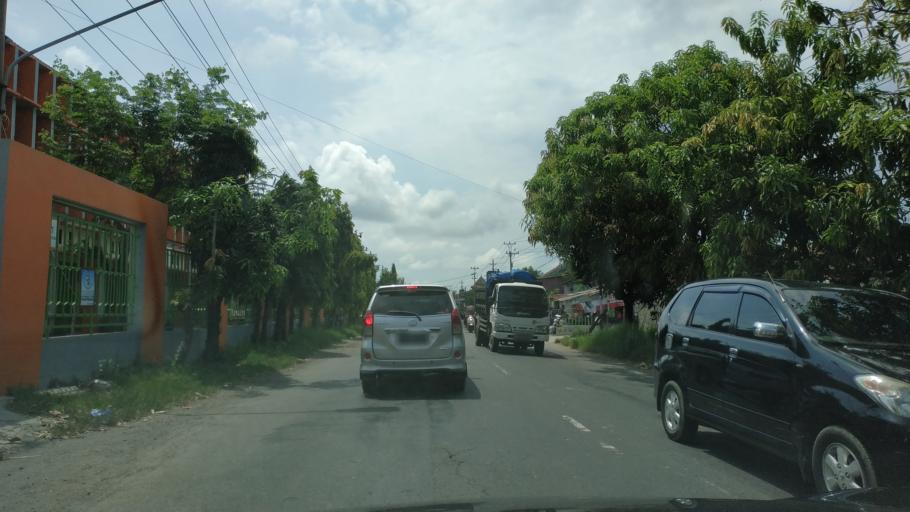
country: ID
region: Central Java
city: Adiwerna
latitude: -6.9215
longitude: 109.1261
